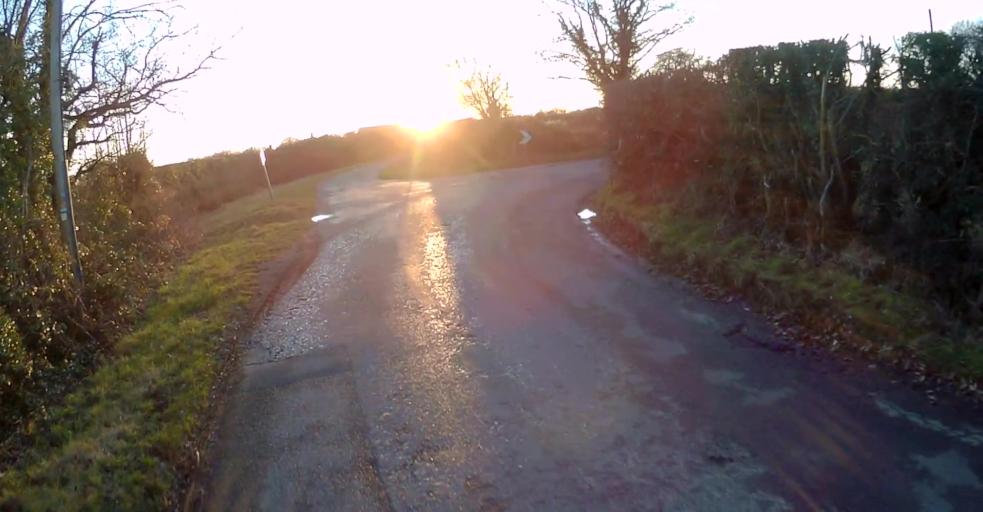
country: GB
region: England
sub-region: West Berkshire
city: Stratfield Mortimer
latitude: 51.3466
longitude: -1.0102
